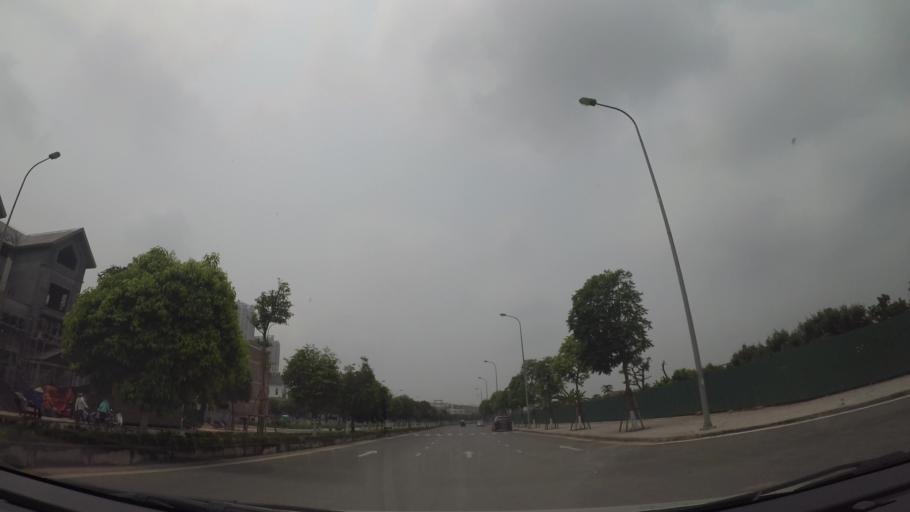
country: VN
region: Ha Noi
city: Ha Dong
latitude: 20.9779
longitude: 105.7582
